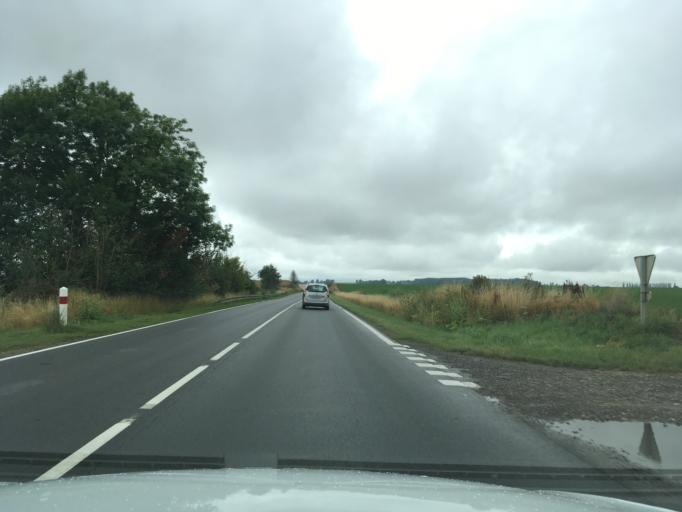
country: FR
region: Picardie
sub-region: Departement de l'Aisne
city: Ribemont
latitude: 49.8419
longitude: 3.4321
